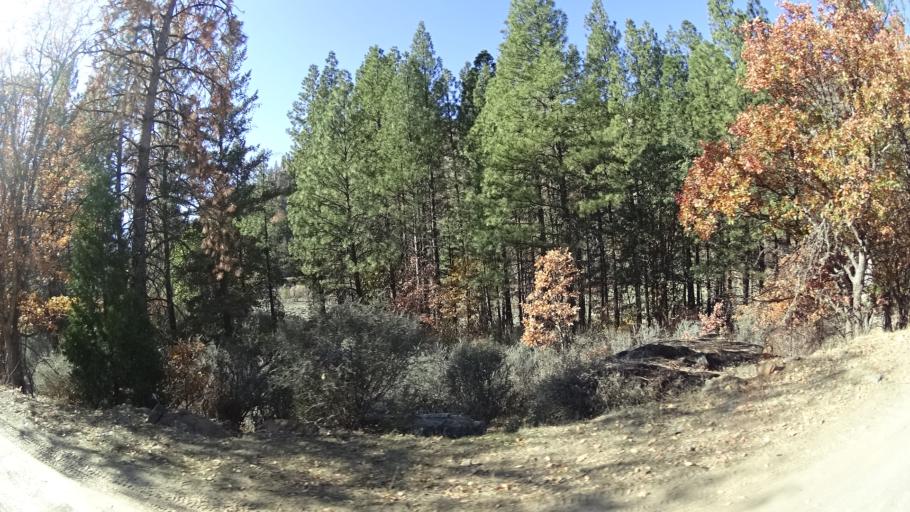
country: US
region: California
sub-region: Siskiyou County
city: Yreka
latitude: 41.8430
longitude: -122.8368
